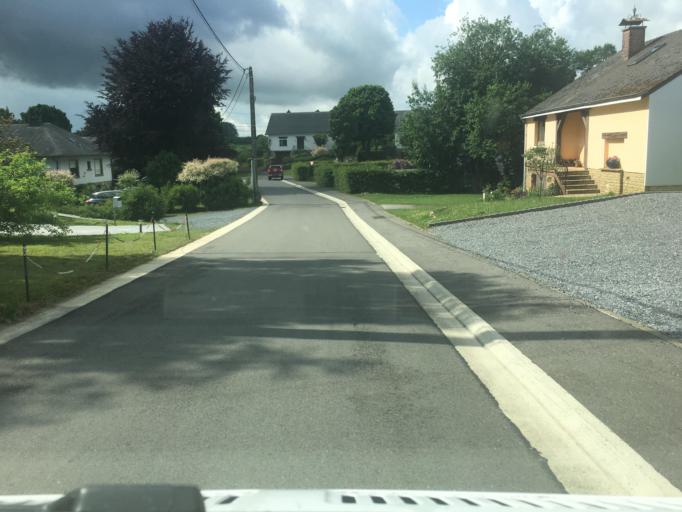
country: BE
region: Wallonia
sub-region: Province du Luxembourg
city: Florenville
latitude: 49.6922
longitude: 5.3206
